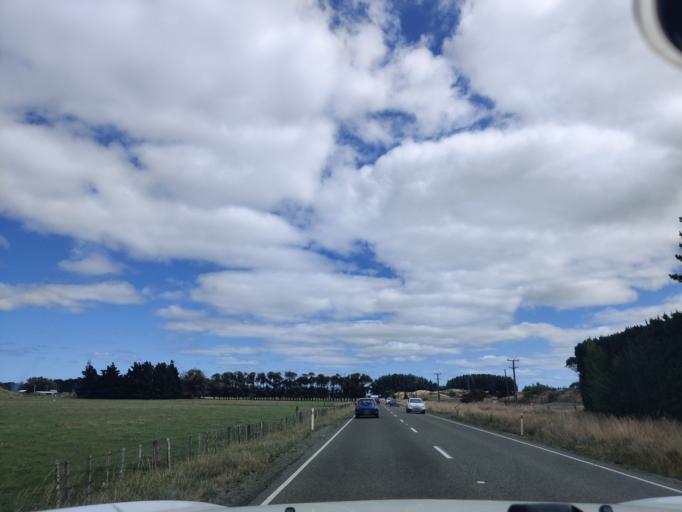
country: NZ
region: Manawatu-Wanganui
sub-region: Horowhenua District
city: Foxton
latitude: -40.4207
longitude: 175.4332
